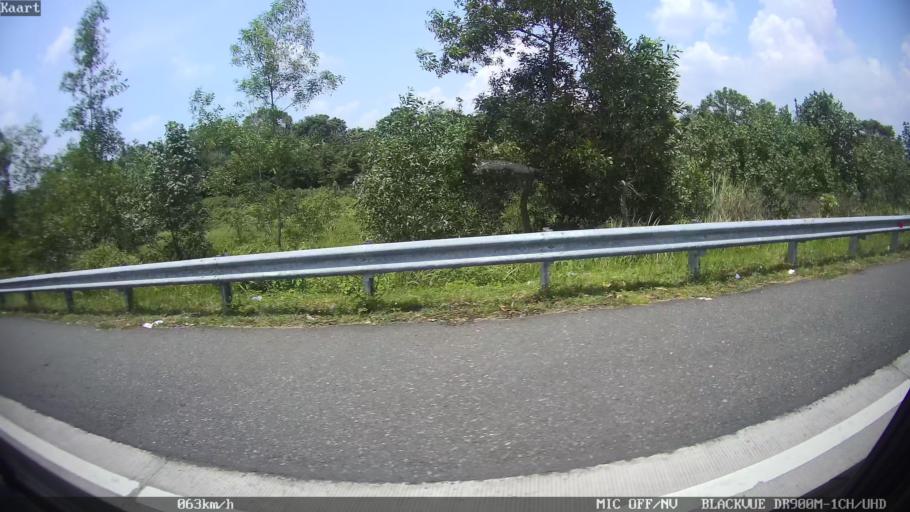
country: ID
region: Lampung
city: Natar
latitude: -5.3047
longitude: 105.2453
